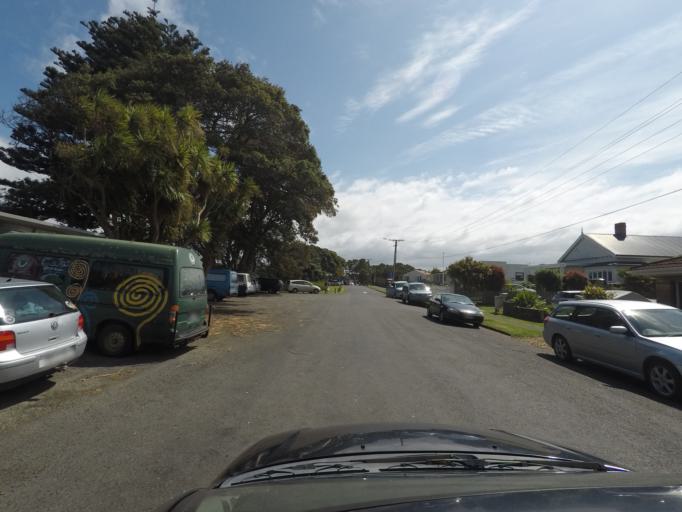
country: NZ
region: Waikato
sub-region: Waikato District
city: Raglan
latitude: -37.7990
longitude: 174.8675
